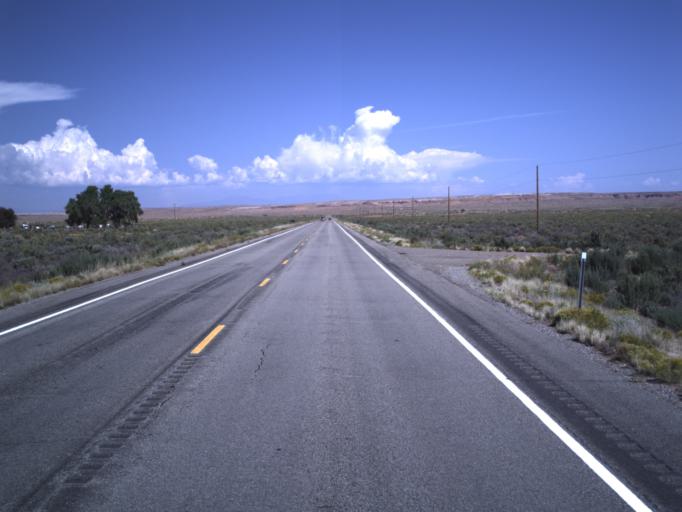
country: US
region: Utah
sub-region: San Juan County
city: Blanding
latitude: 37.0995
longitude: -109.5473
